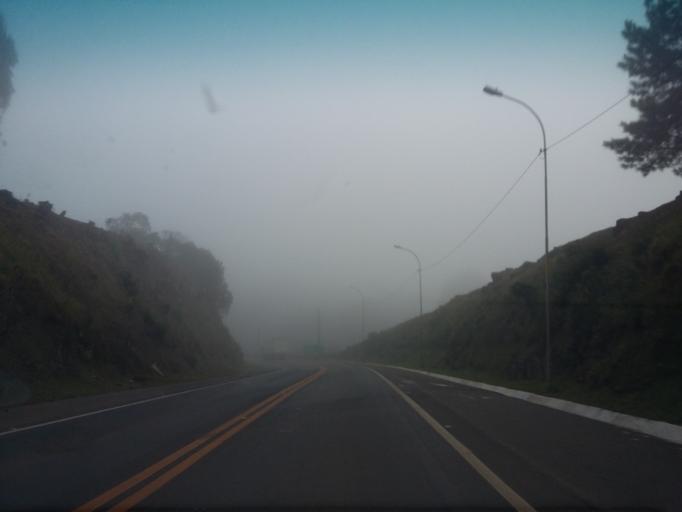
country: BR
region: Santa Catarina
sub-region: Curitibanos
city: Curitibanos
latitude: -27.2648
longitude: -50.4421
